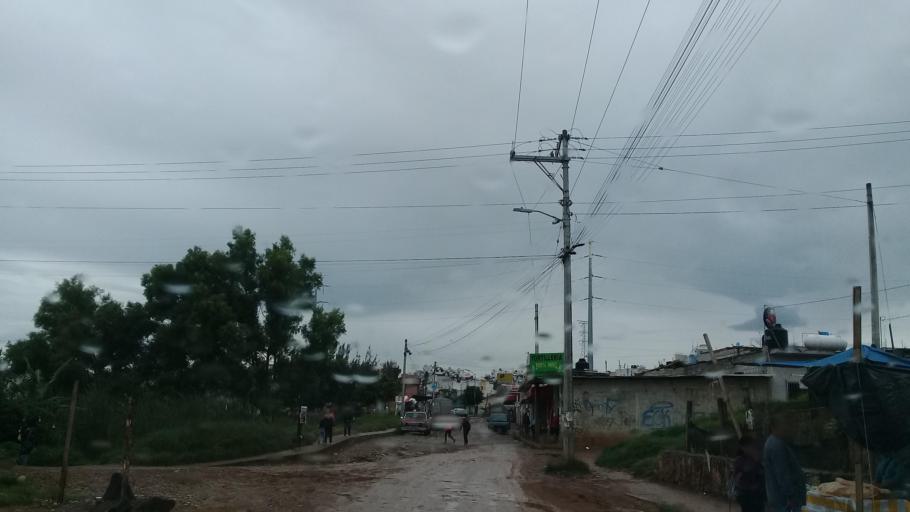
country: MX
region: Veracruz
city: El Castillo
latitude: 19.5665
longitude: -96.8887
